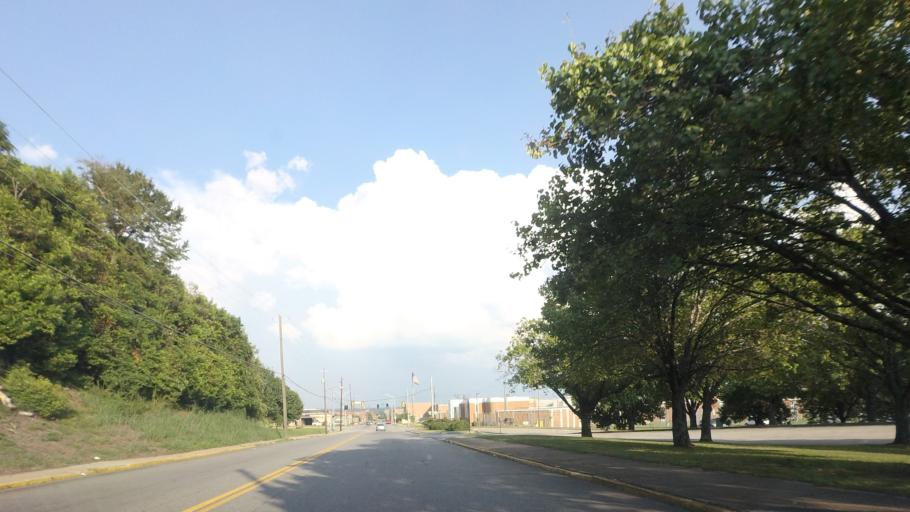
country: US
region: Georgia
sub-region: Bibb County
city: Macon
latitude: 32.8302
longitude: -83.6388
